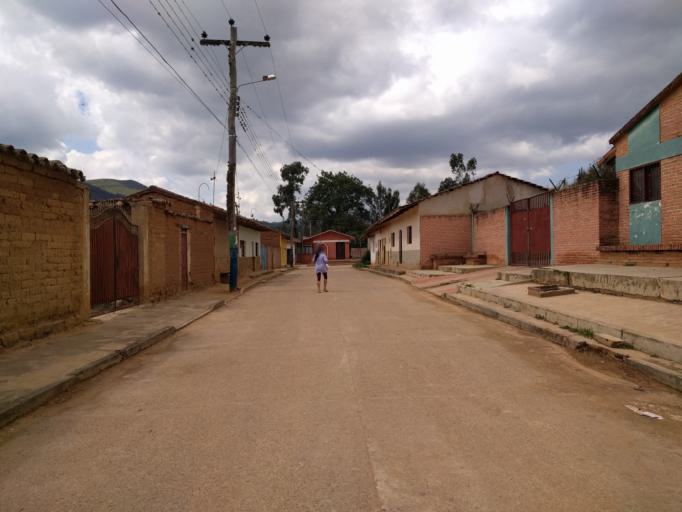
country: BO
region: Santa Cruz
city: Samaipata
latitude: -18.1821
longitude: -63.8762
